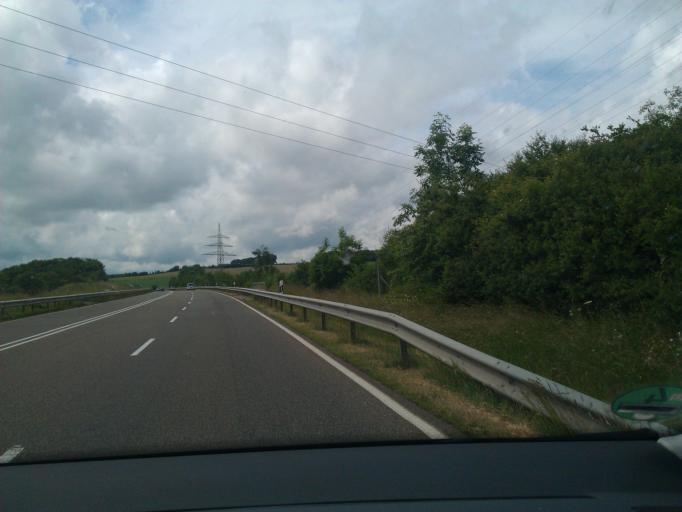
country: DE
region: Rheinland-Pfalz
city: Watzerath
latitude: 50.1968
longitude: 6.3727
